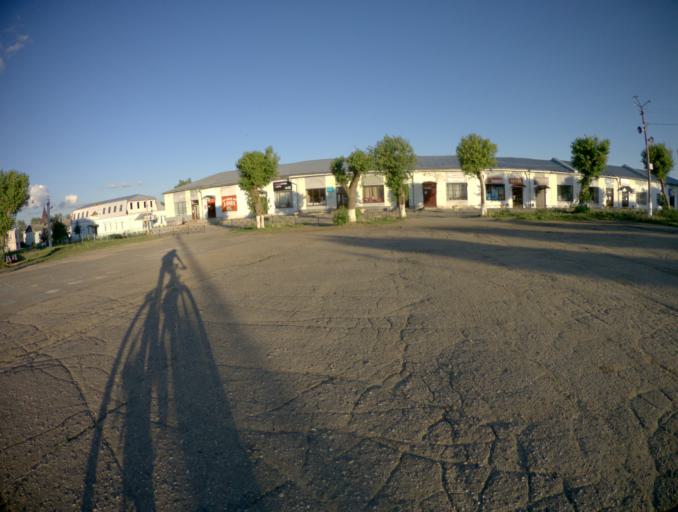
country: RU
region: Ivanovo
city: Gavrilov Posad
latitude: 56.5585
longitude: 40.1205
